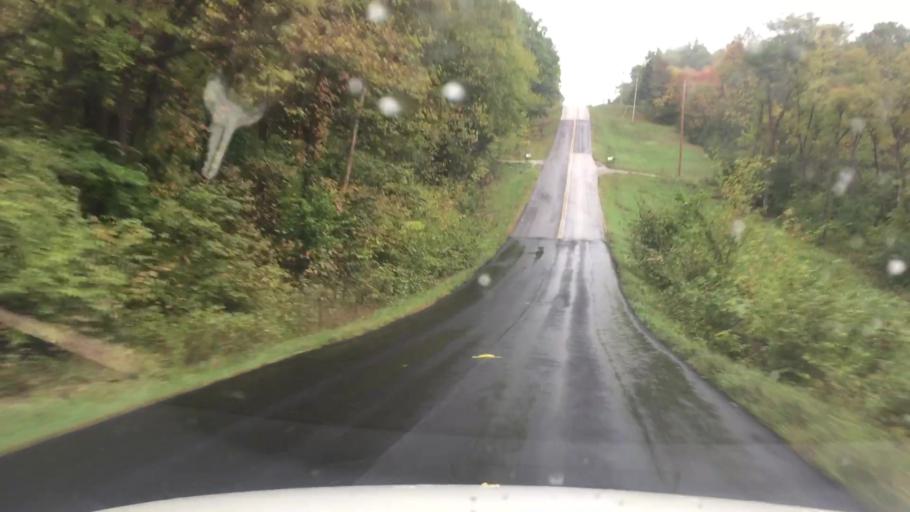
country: US
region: Missouri
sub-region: Boone County
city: Columbia
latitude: 38.9488
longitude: -92.4961
